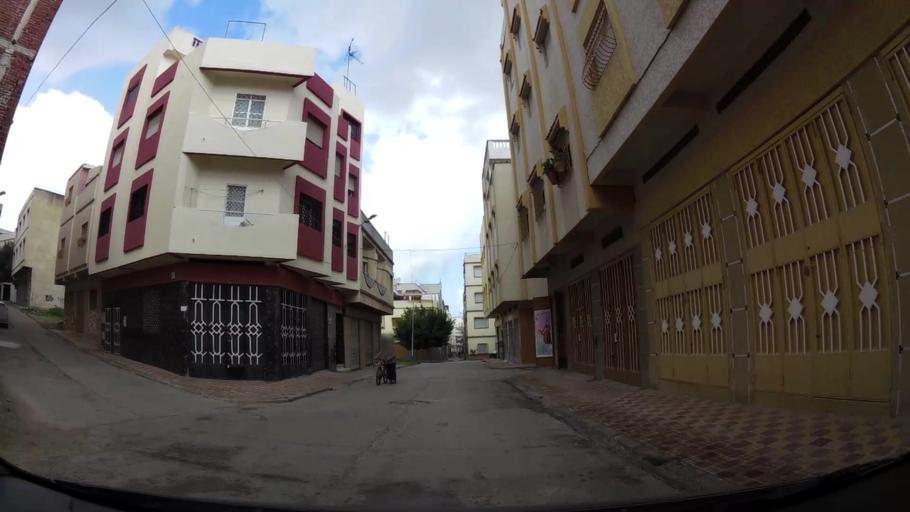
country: MA
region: Tanger-Tetouan
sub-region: Tanger-Assilah
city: Tangier
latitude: 35.7573
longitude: -5.8182
